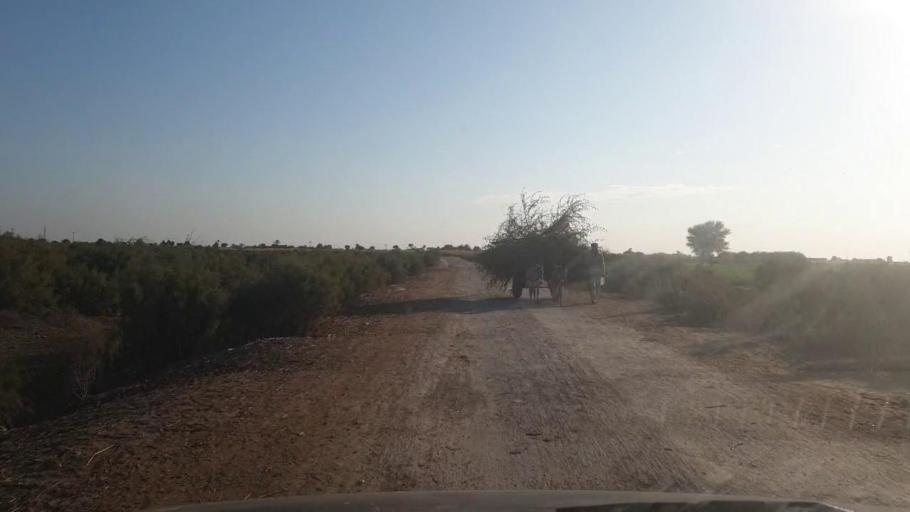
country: PK
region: Sindh
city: Sinjhoro
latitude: 26.0513
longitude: 68.8711
